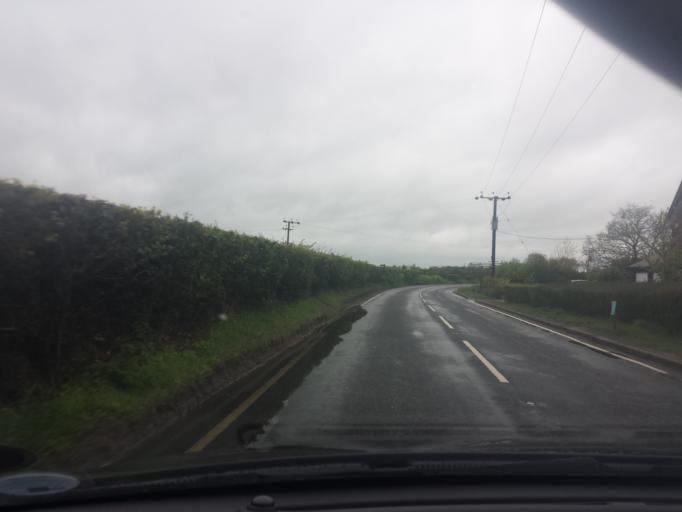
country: GB
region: England
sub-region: Essex
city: Alresford
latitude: 51.8993
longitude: 1.0149
